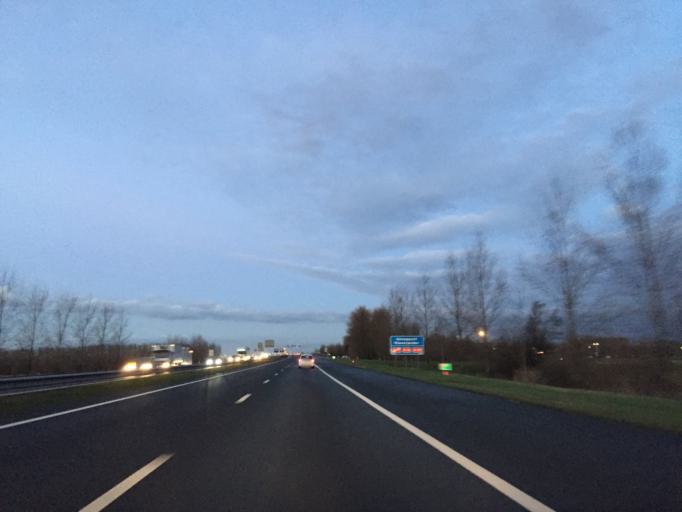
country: NL
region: South Holland
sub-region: Gemeente Strijen
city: Strijen
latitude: 51.6906
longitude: 4.6382
